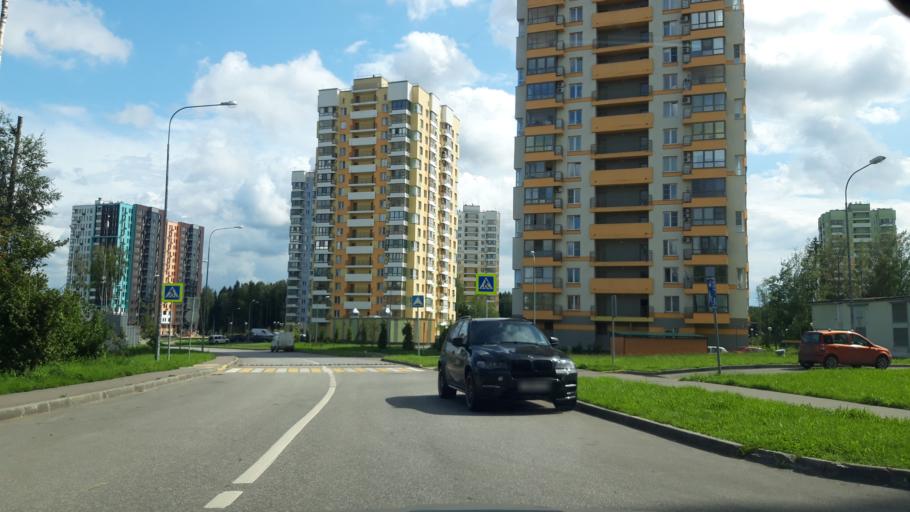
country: RU
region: Moscow
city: Zelenograd
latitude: 55.9675
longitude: 37.1891
